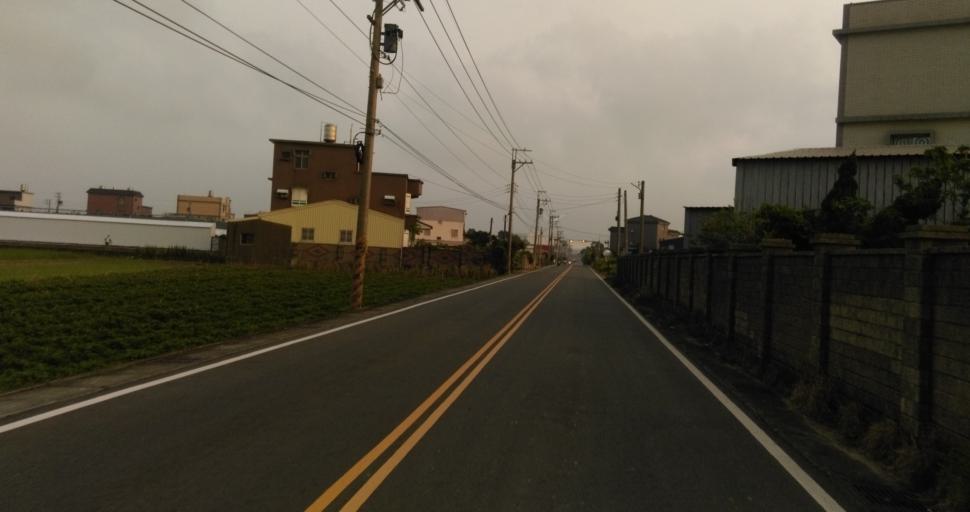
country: TW
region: Taiwan
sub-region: Hsinchu
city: Zhubei
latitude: 24.8673
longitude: 120.9591
